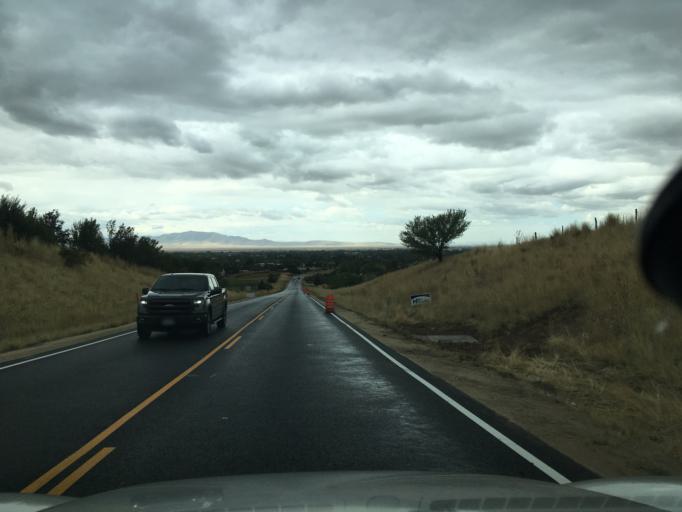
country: US
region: Utah
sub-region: Davis County
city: Kaysville
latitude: 41.0639
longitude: -111.9269
